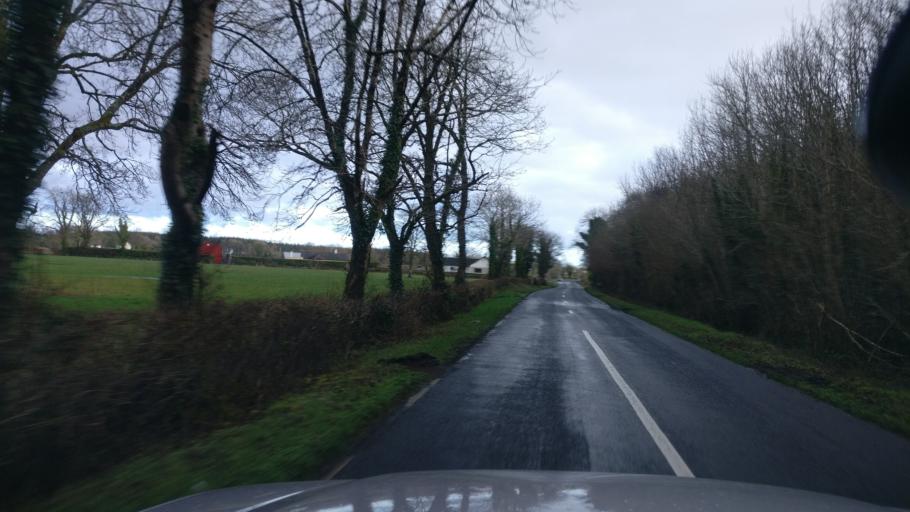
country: IE
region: Connaught
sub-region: County Galway
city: Athenry
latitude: 53.2957
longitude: -8.6541
